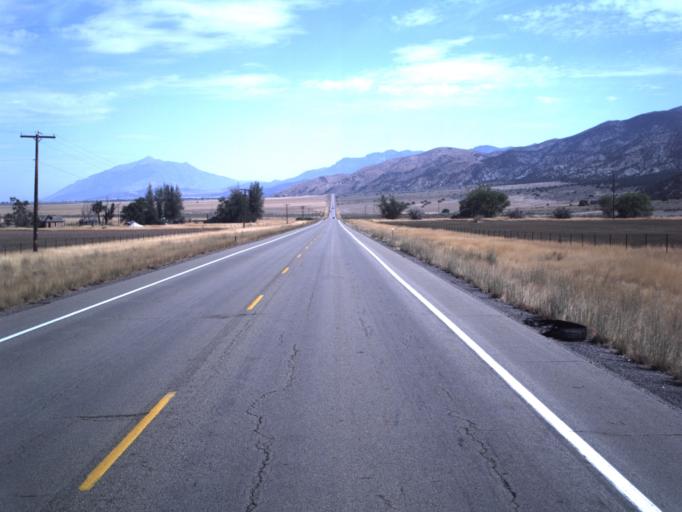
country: US
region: Utah
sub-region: Juab County
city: Nephi
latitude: 39.4727
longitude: -111.8948
